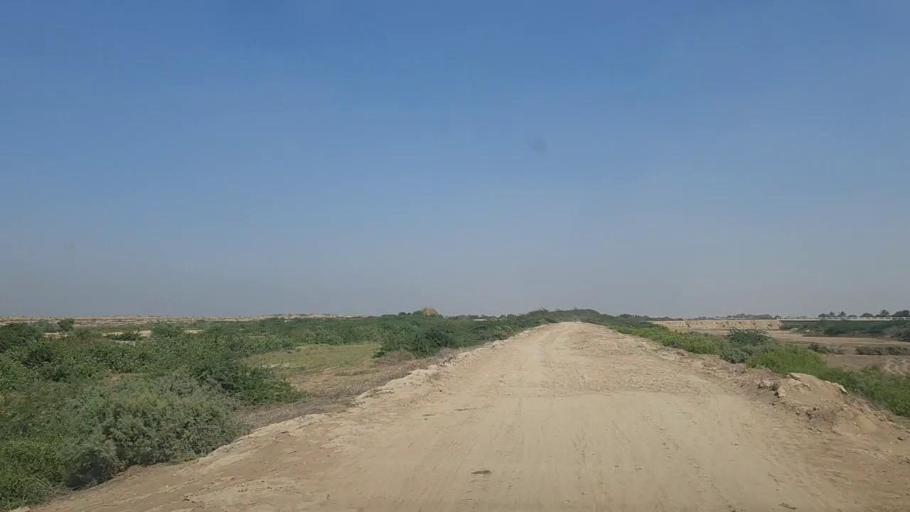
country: PK
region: Sindh
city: Thatta
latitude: 24.8468
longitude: 68.0249
